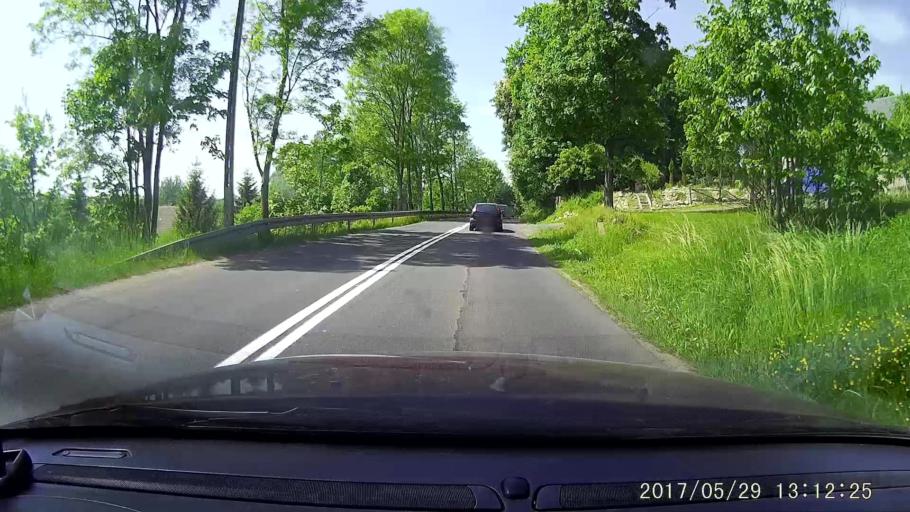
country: PL
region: Lower Silesian Voivodeship
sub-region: Powiat lwowecki
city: Lubomierz
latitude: 50.9682
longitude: 15.5072
